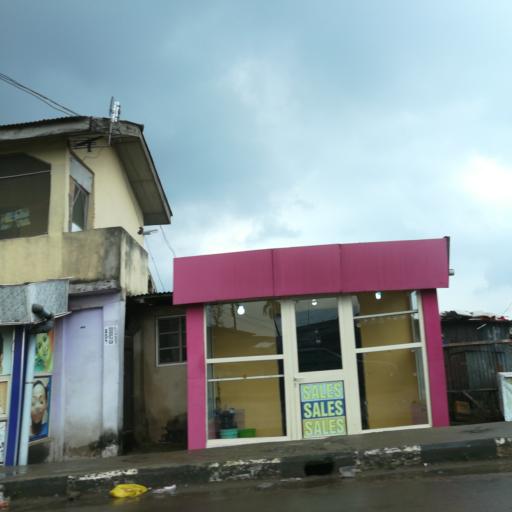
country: NG
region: Lagos
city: Agege
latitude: 6.5938
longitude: 3.2938
